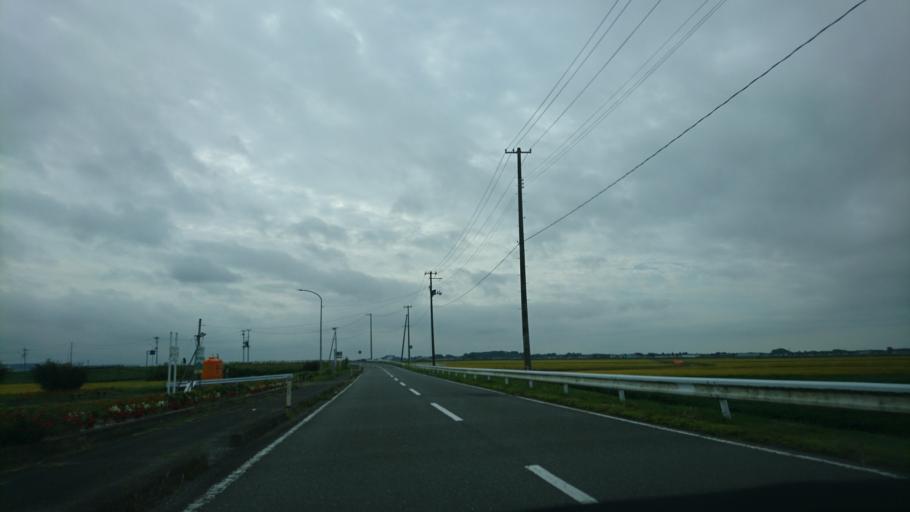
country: JP
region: Iwate
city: Ichinoseki
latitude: 38.8047
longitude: 141.1123
